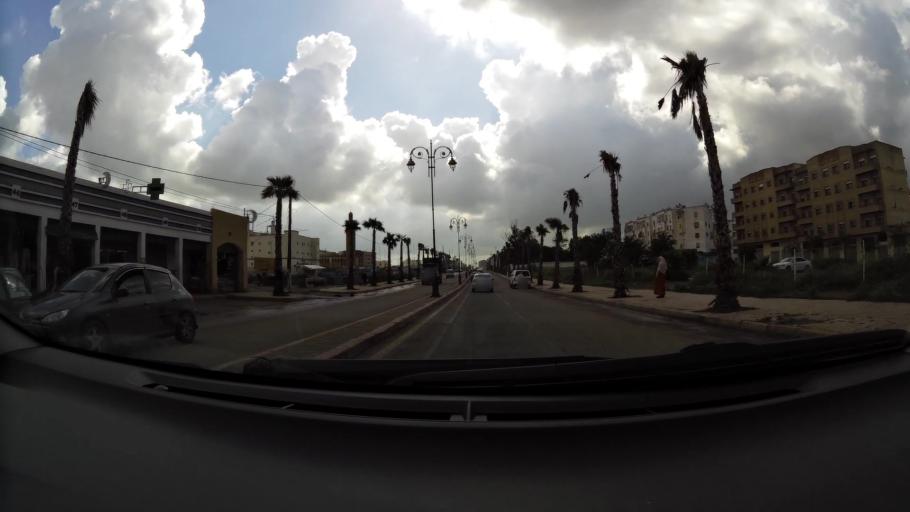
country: MA
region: Grand Casablanca
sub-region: Mediouna
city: Tit Mellil
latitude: 33.5552
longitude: -7.4813
